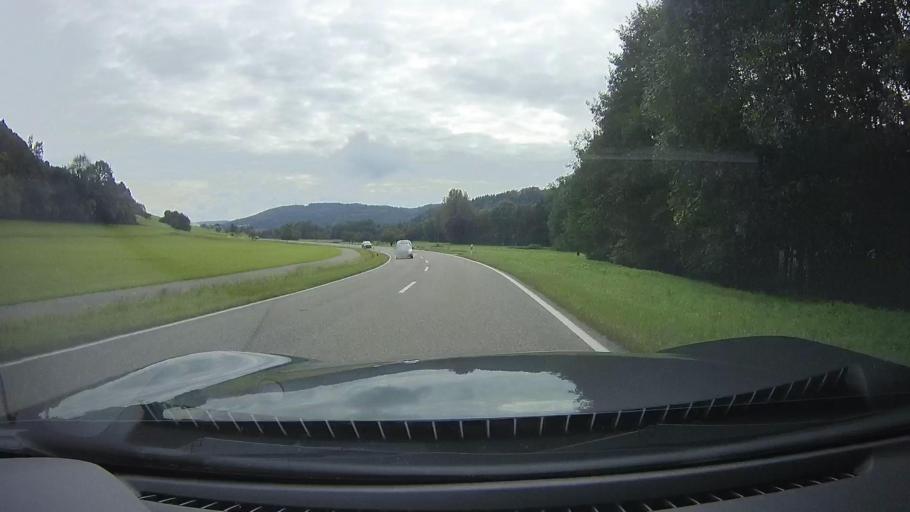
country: DE
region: Baden-Wuerttemberg
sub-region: Regierungsbezirk Stuttgart
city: Sulzbach an der Murr
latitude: 49.0131
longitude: 9.4750
